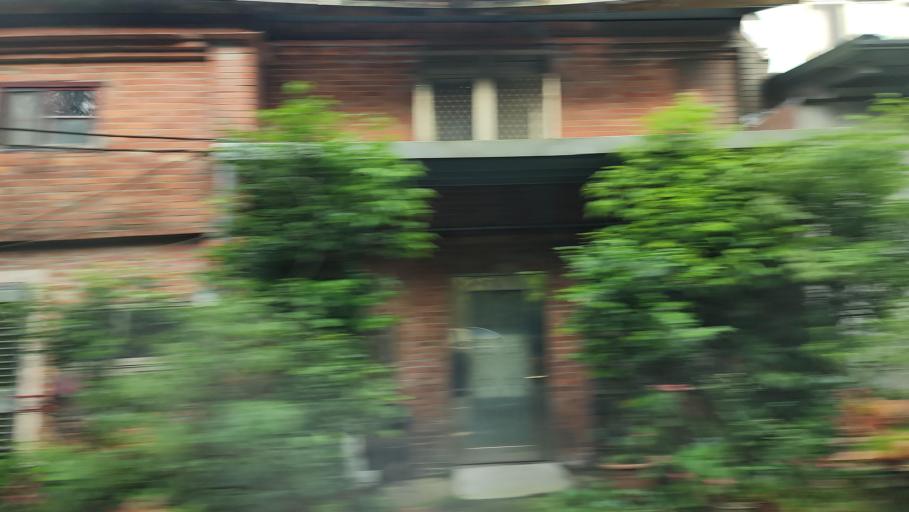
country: TW
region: Taiwan
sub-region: Keelung
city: Keelung
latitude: 25.1566
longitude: 121.6461
